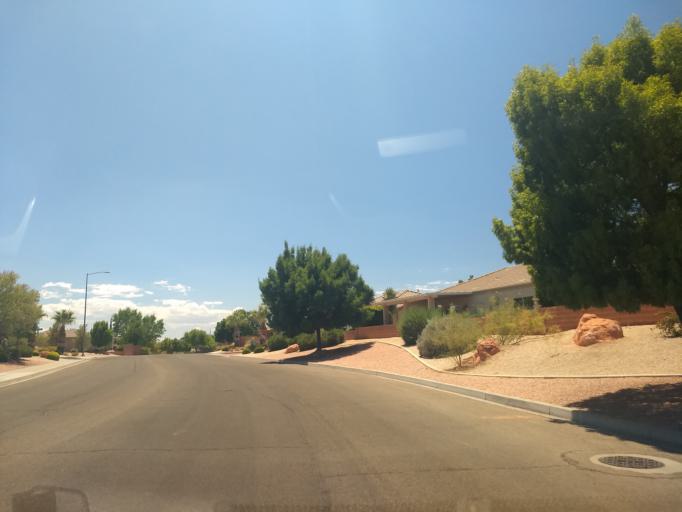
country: US
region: Utah
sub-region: Washington County
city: Washington
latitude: 37.1468
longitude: -113.5238
